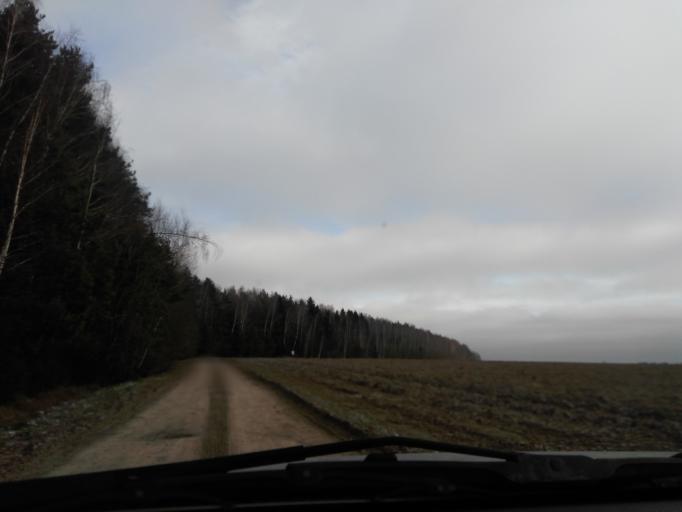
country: RU
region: Moskovskaya
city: Troitsk
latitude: 55.3669
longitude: 37.1742
